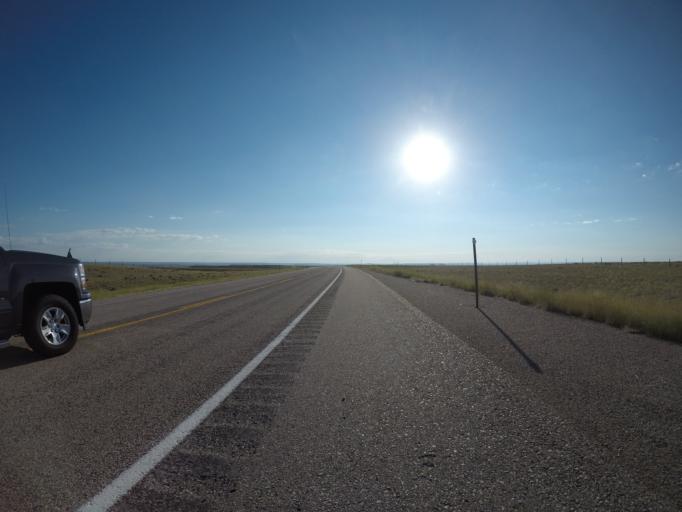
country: US
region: Wyoming
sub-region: Lincoln County
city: Kemmerer
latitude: 41.8950
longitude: -110.3374
